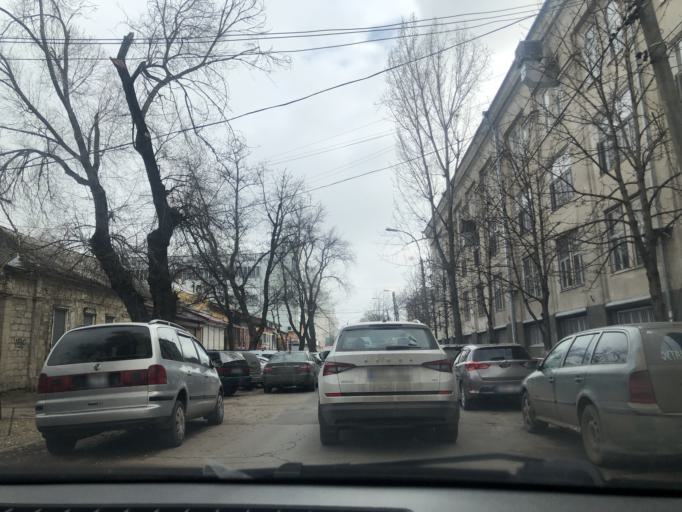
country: MD
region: Chisinau
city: Chisinau
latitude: 47.0213
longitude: 28.8439
